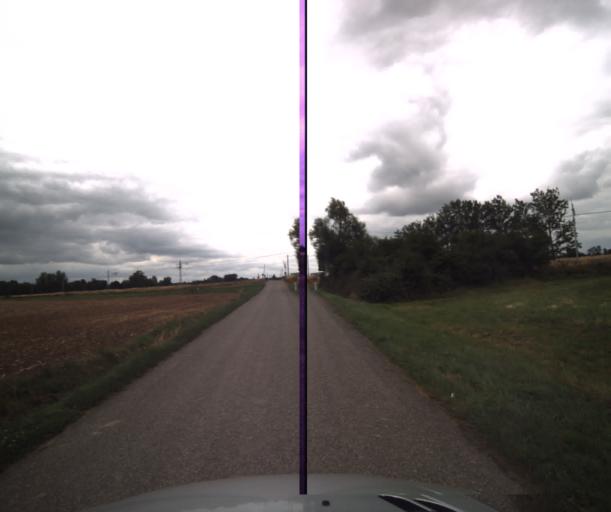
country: FR
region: Midi-Pyrenees
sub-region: Departement de la Haute-Garonne
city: Labarthe-sur-Leze
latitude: 43.4638
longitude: 1.4090
